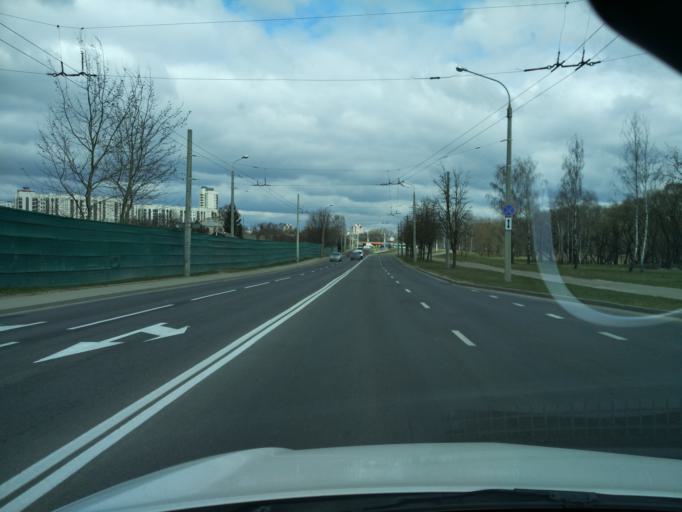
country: BY
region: Minsk
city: Novoye Medvezhino
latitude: 53.8659
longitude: 27.4960
